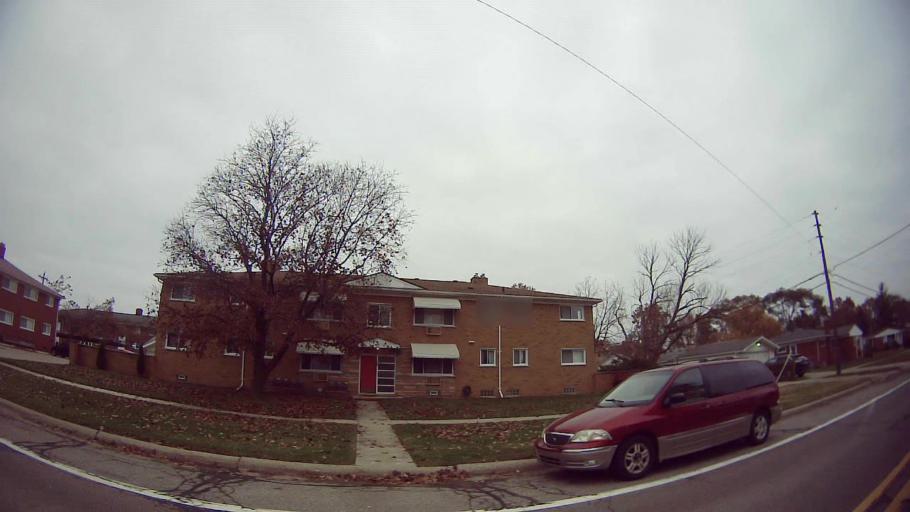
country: US
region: Michigan
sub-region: Oakland County
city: Madison Heights
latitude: 42.4984
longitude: -83.1204
